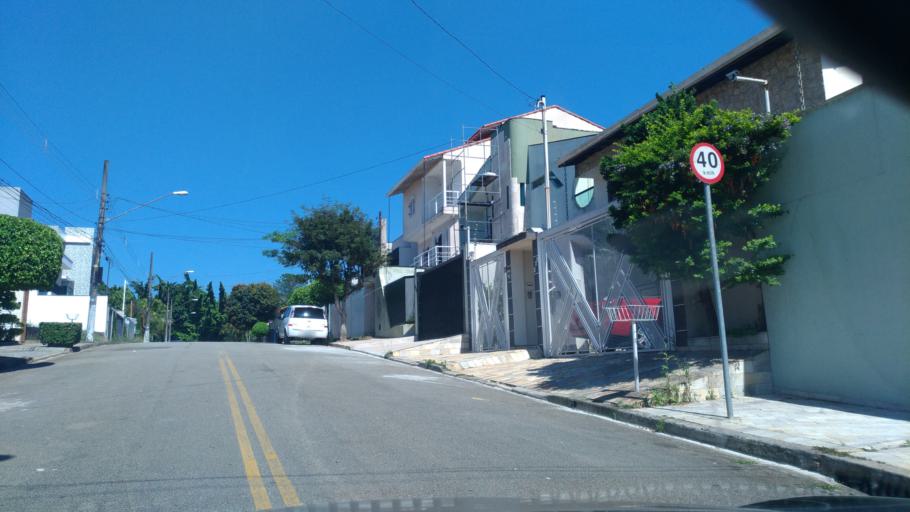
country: BR
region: Sao Paulo
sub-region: Sao Bernardo Do Campo
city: Sao Bernardo do Campo
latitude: -23.7072
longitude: -46.5792
